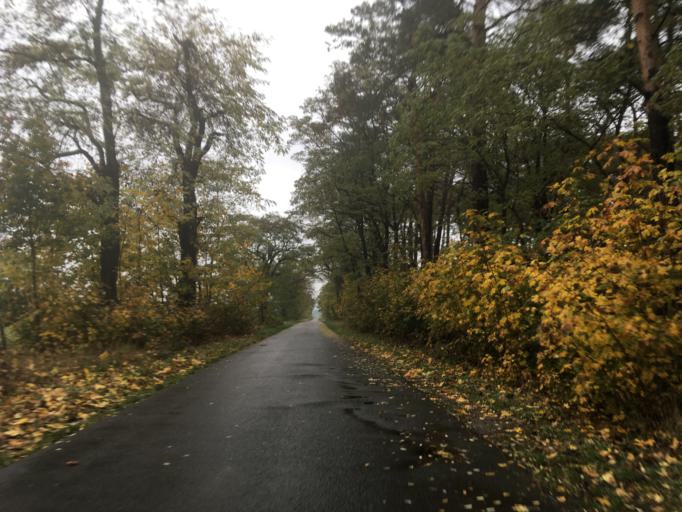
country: DE
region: Brandenburg
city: Neu Zauche
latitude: 52.0261
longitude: 14.1082
